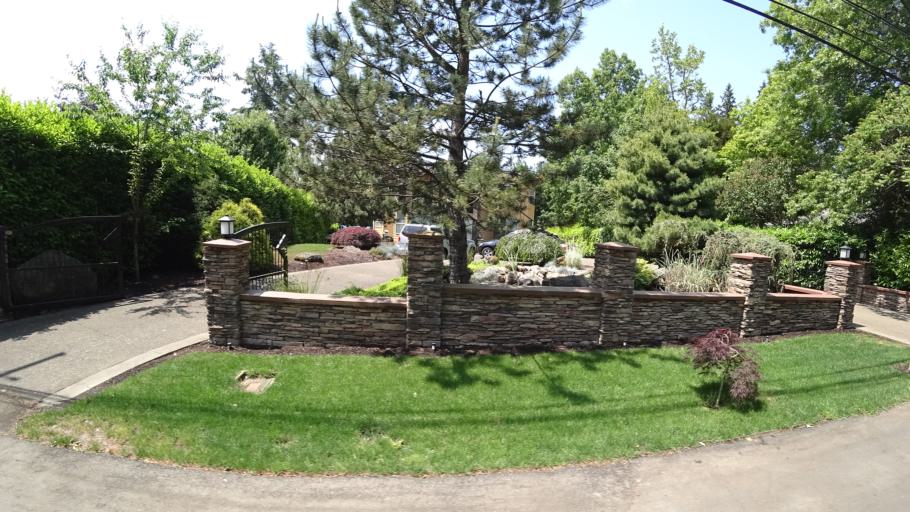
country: US
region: Oregon
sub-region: Clackamas County
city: Happy Valley
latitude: 45.4530
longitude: -122.5482
